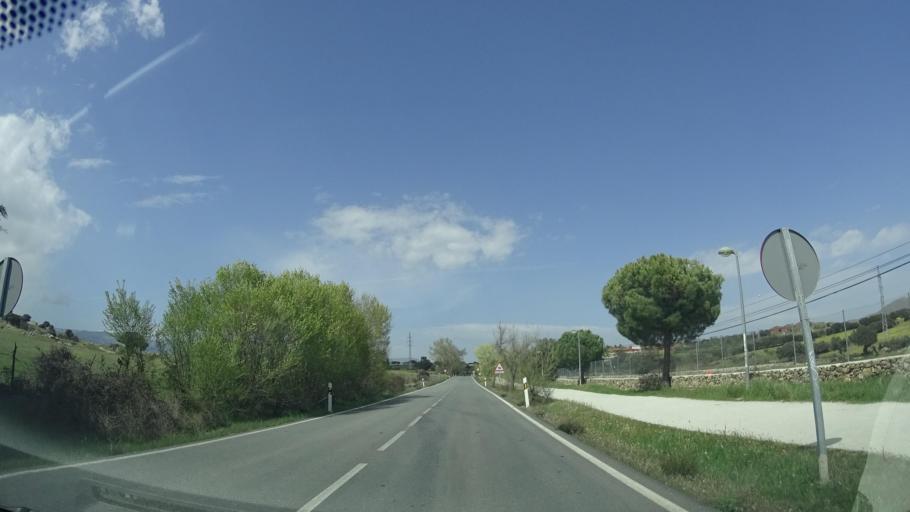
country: ES
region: Madrid
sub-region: Provincia de Madrid
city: Colmenar Viejo
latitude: 40.6882
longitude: -3.7697
